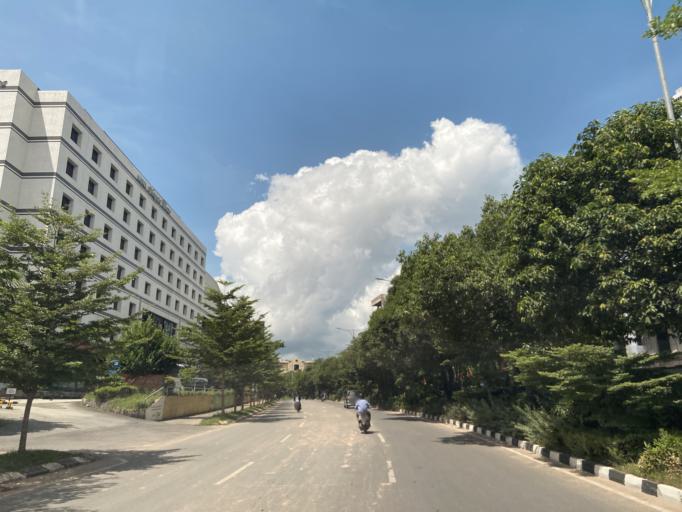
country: SG
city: Singapore
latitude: 1.1465
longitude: 104.0104
